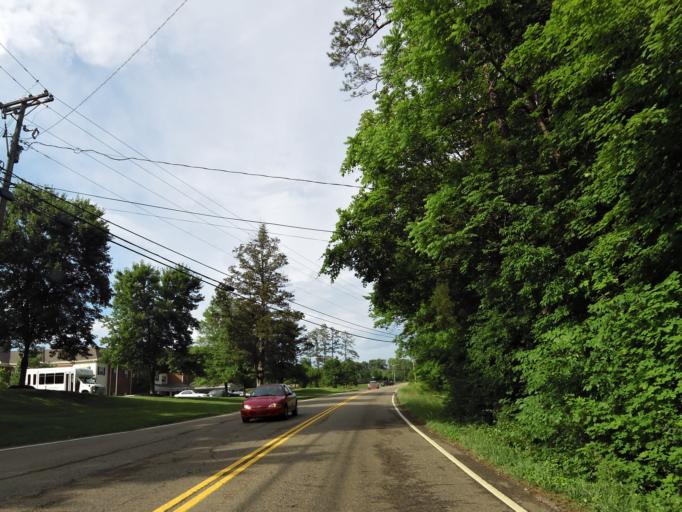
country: US
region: Tennessee
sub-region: Blount County
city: Louisville
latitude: 35.8933
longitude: -84.0335
